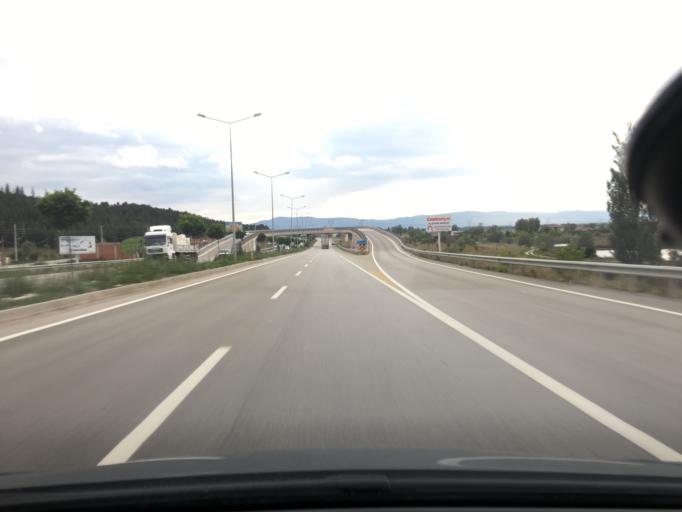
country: TR
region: Afyonkarahisar
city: Sincanli
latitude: 38.7919
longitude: 30.3838
